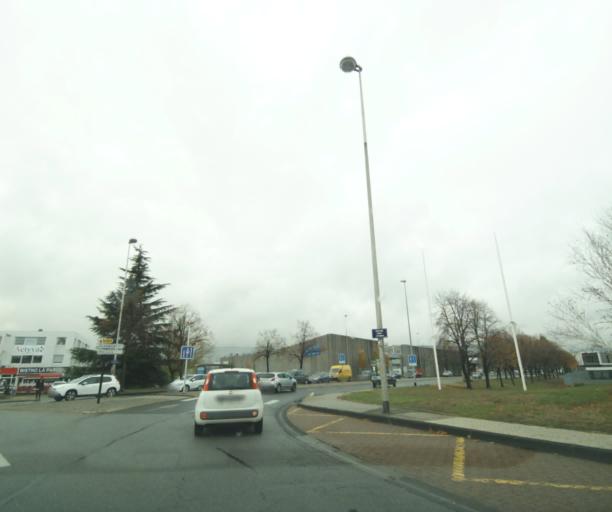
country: FR
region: Auvergne
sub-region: Departement du Puy-de-Dome
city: Aubiere
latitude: 45.7614
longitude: 3.1320
